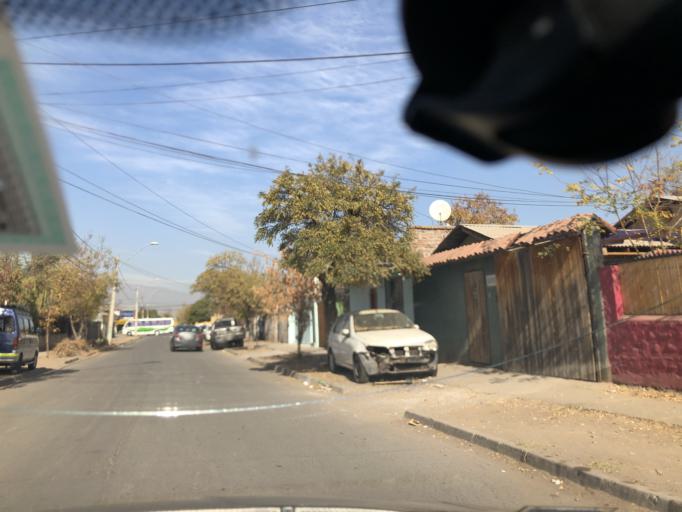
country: CL
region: Santiago Metropolitan
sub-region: Provincia de Cordillera
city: Puente Alto
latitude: -33.6149
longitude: -70.5716
